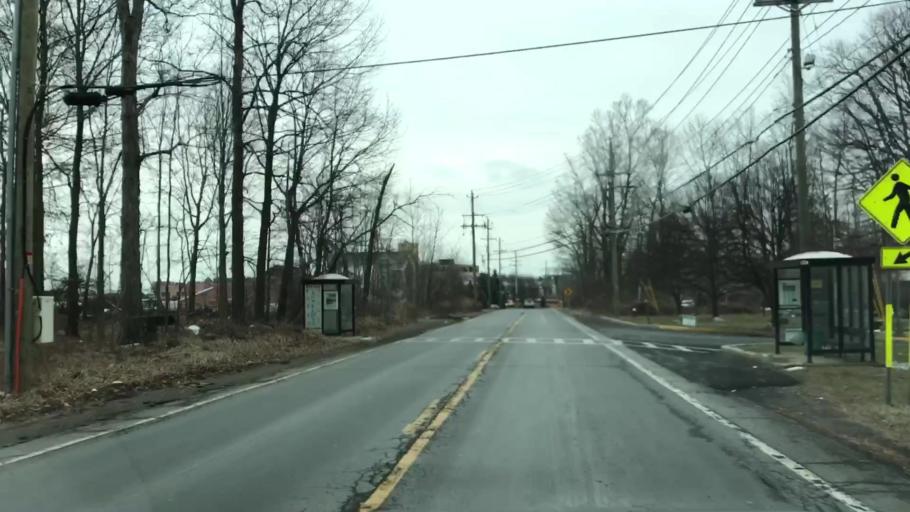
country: US
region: New York
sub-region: Rockland County
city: New Hempstead
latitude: 41.1446
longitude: -74.0343
